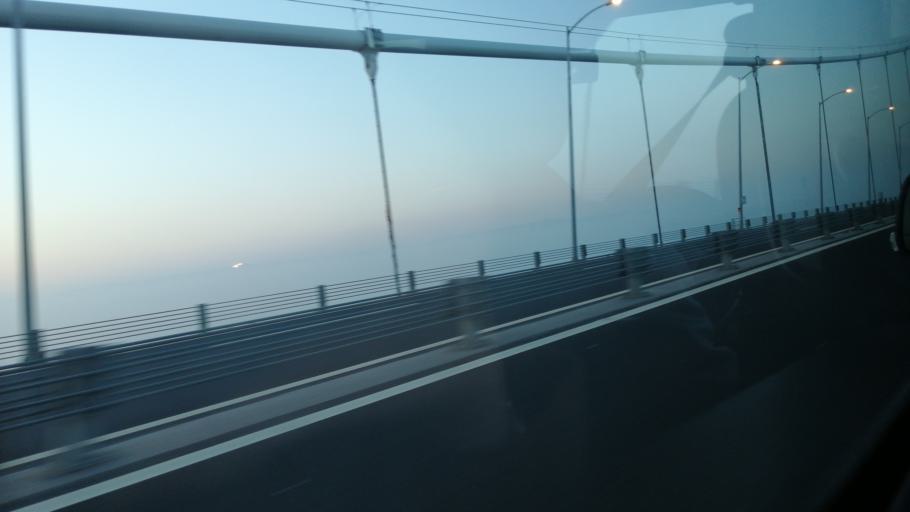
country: TR
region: Kocaeli
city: Tavsancil
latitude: 40.7559
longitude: 29.5161
